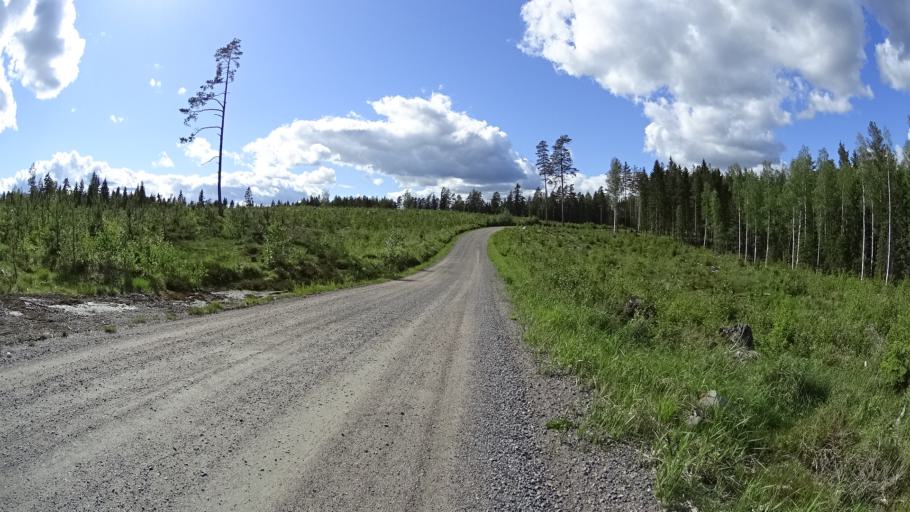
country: FI
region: Varsinais-Suomi
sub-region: Salo
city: Kisko
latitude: 60.1902
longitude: 23.5588
